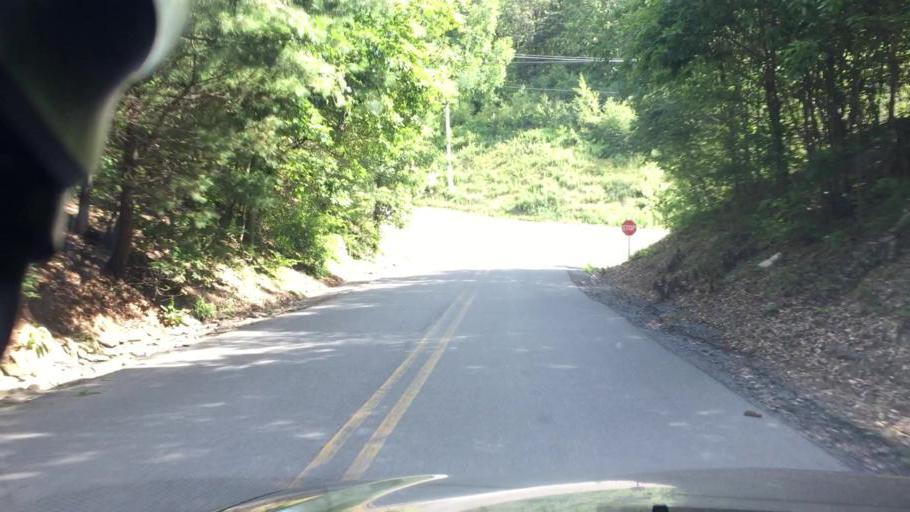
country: US
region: Pennsylvania
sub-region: Luzerne County
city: Oakdale
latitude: 41.0184
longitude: -75.9278
